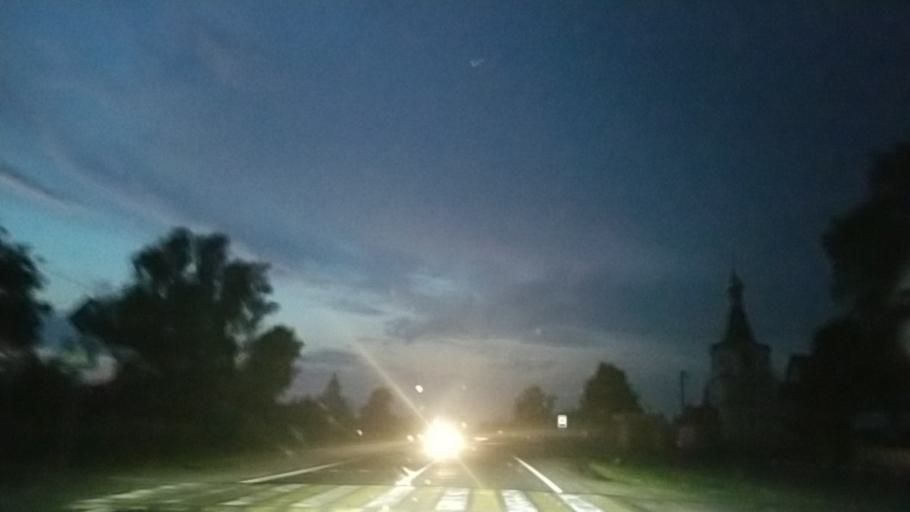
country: PL
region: Lublin Voivodeship
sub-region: Powiat bialski
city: Koden
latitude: 51.9296
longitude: 23.6600
